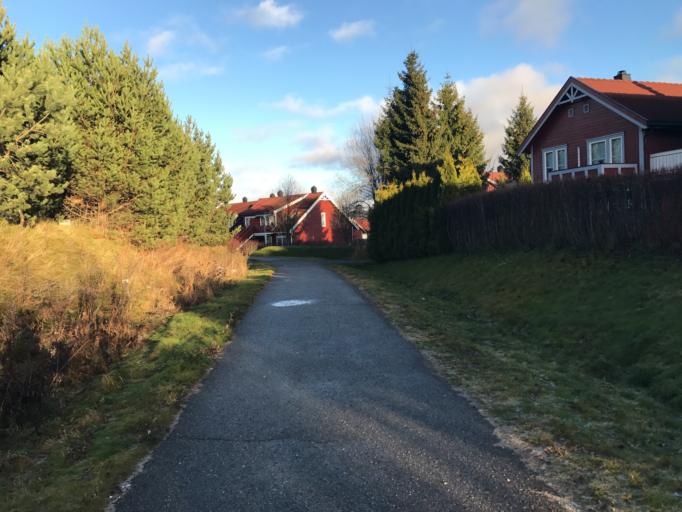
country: NO
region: Akershus
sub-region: Ullensaker
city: Jessheim
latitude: 60.1388
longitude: 11.1903
